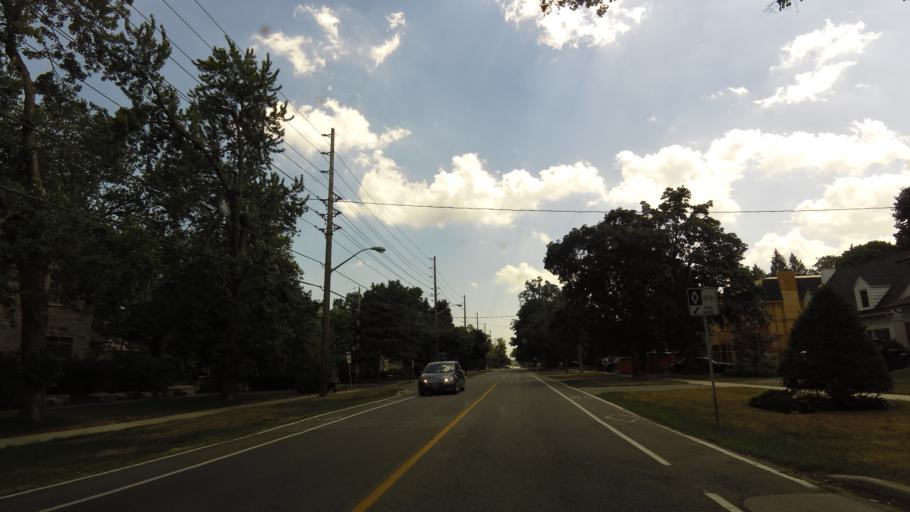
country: CA
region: Ontario
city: Etobicoke
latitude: 43.6689
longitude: -79.5209
